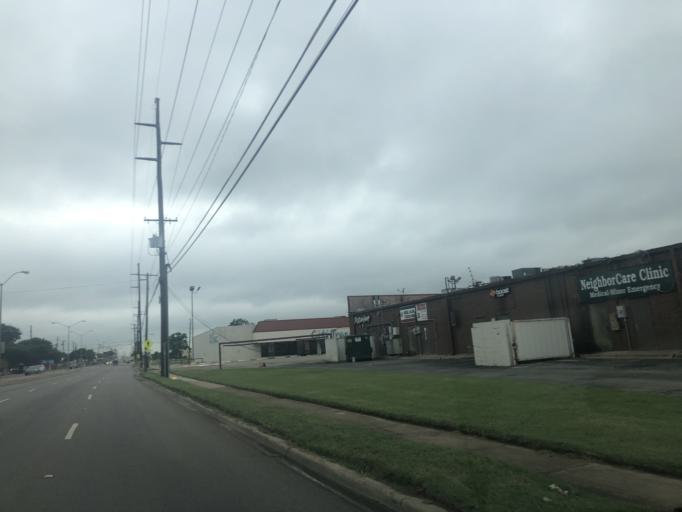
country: US
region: Texas
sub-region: Dallas County
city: Cockrell Hill
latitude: 32.7788
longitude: -96.8587
